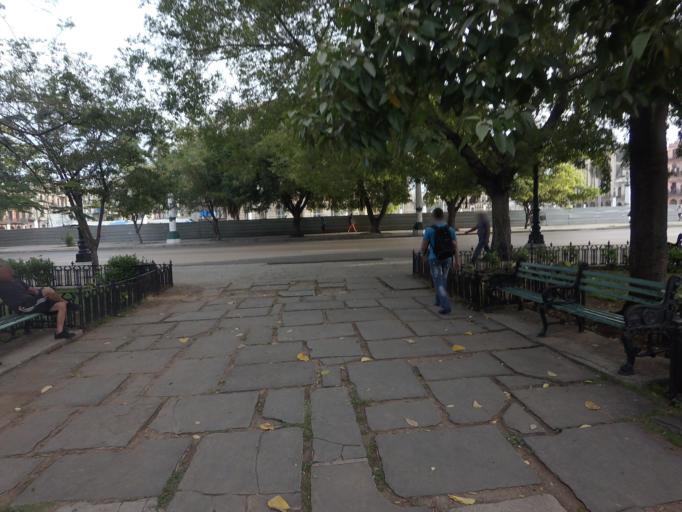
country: CU
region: La Habana
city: Centro Habana
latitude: 23.1335
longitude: -82.3595
